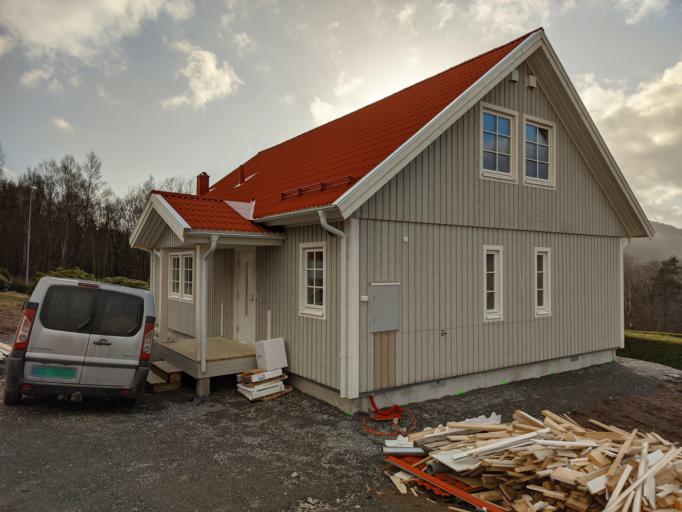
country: NO
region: Hordaland
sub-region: Etne
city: Etne
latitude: 59.8603
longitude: 5.7710
